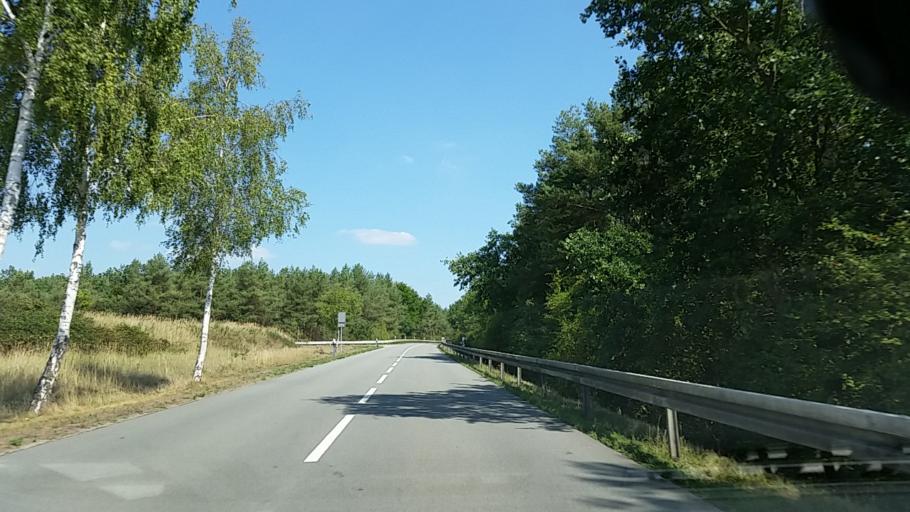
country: DE
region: Lower Saxony
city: Bienenbuttel
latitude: 53.1692
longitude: 10.5156
